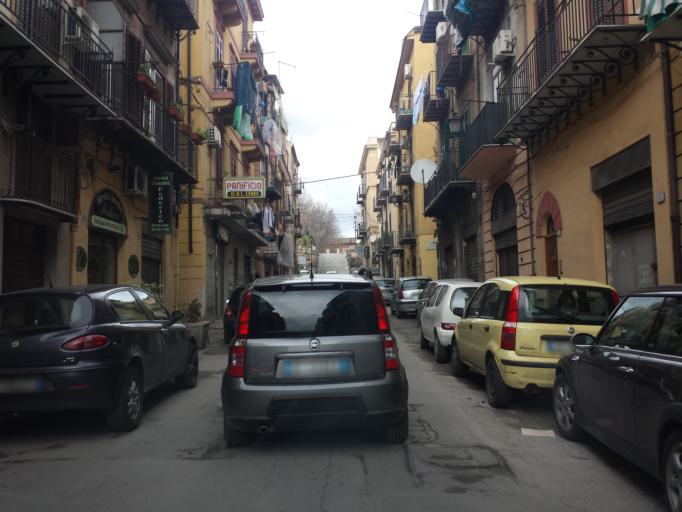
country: IT
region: Sicily
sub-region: Palermo
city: Palermo
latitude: 38.1108
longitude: 13.3556
